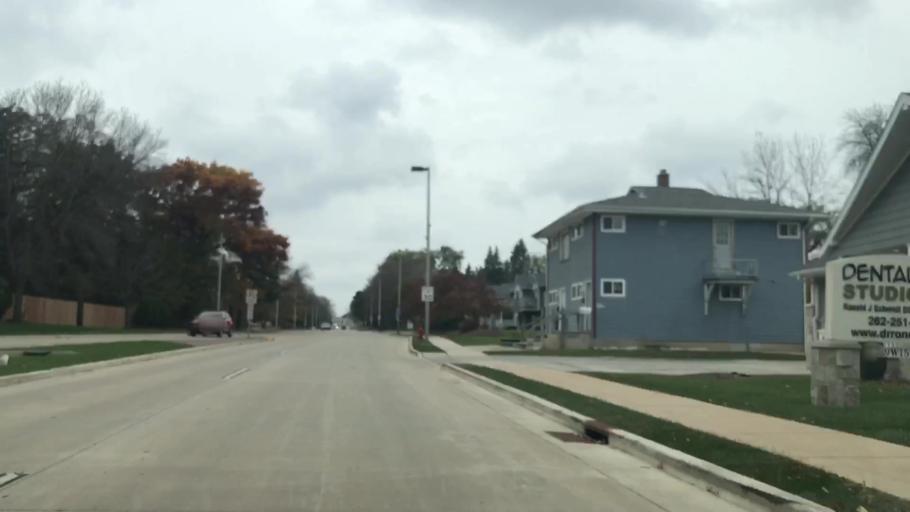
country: US
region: Wisconsin
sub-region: Waukesha County
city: Menomonee Falls
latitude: 43.1793
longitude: -88.1047
